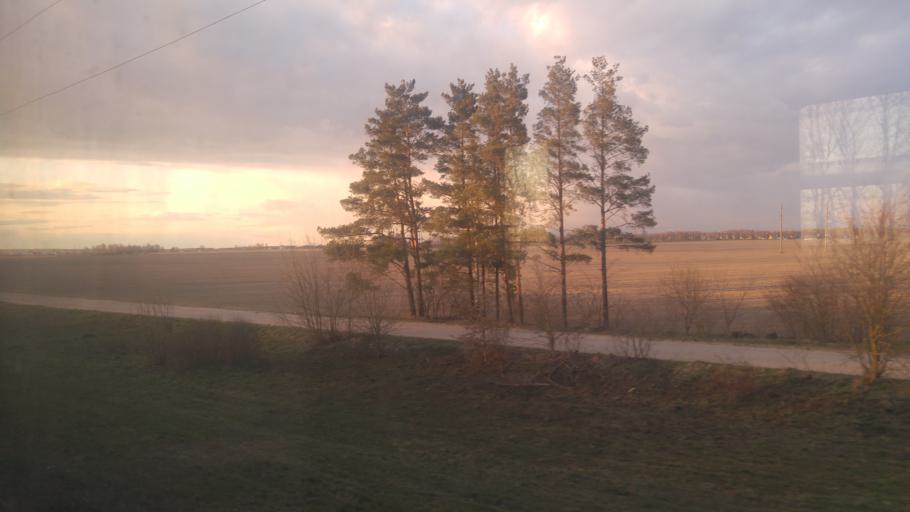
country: BY
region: Minsk
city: Rudzyensk
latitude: 53.6429
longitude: 27.7882
